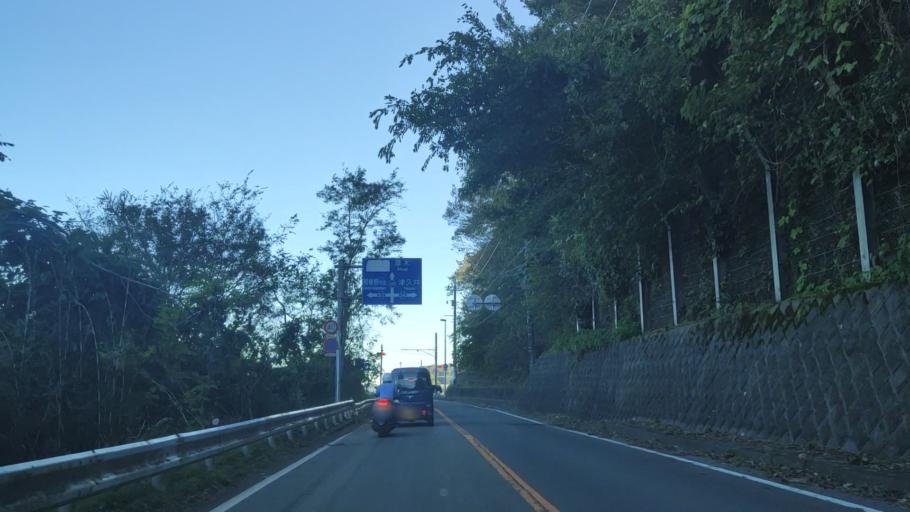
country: JP
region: Kanagawa
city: Zama
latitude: 35.5407
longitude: 139.3281
